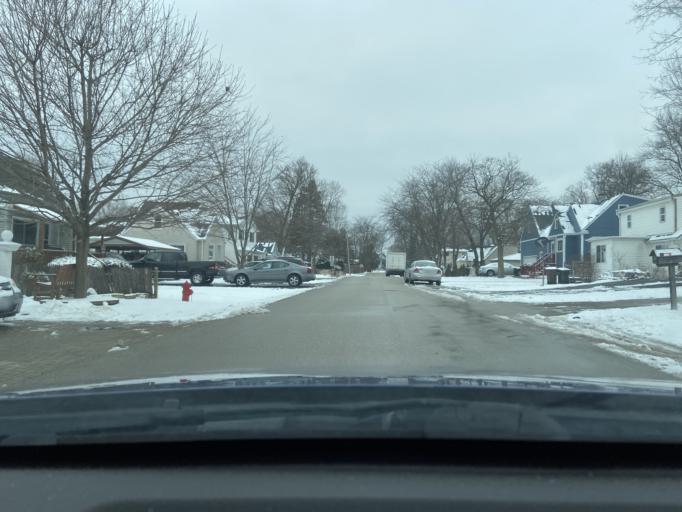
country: US
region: Illinois
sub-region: Lake County
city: Round Lake Park
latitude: 42.3561
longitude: -88.0807
